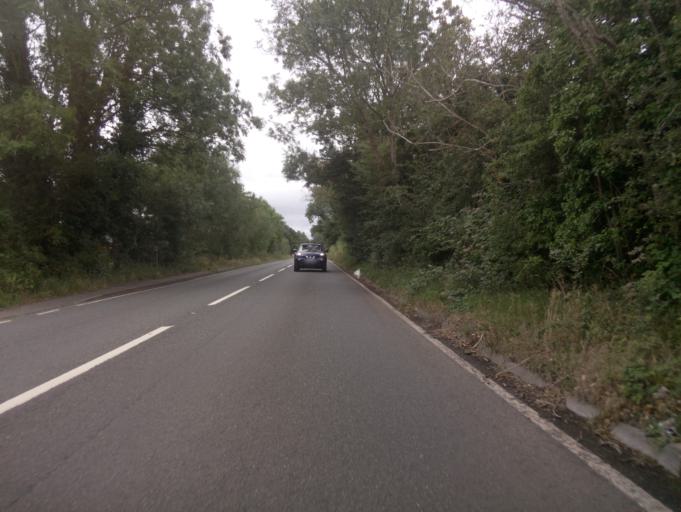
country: GB
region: England
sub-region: Gloucestershire
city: Tewkesbury
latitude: 52.0209
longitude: -2.1646
